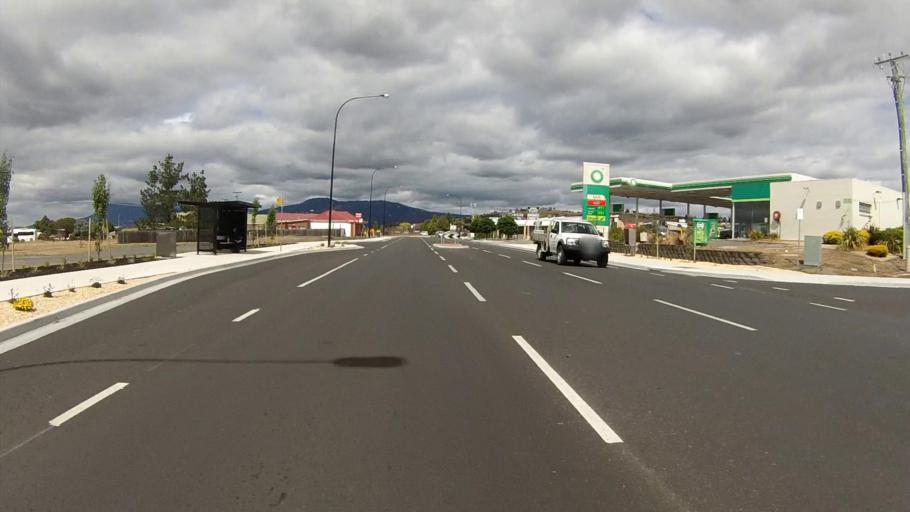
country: AU
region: Tasmania
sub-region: Brighton
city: Bridgewater
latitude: -42.6989
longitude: 147.2521
